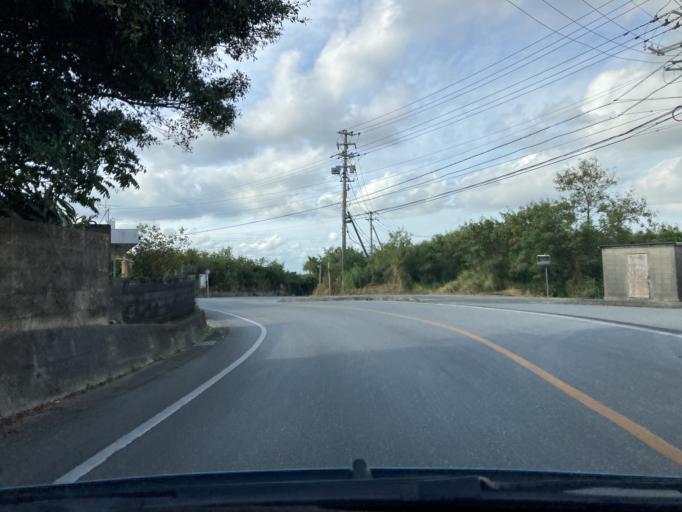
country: JP
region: Okinawa
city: Itoman
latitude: 26.1309
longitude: 127.7111
